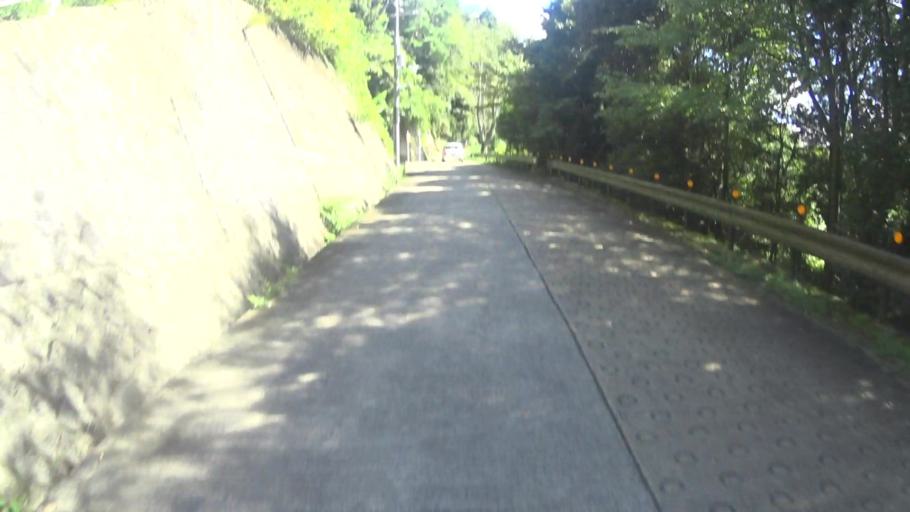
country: JP
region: Nara
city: Nara-shi
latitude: 34.7547
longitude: 135.9386
